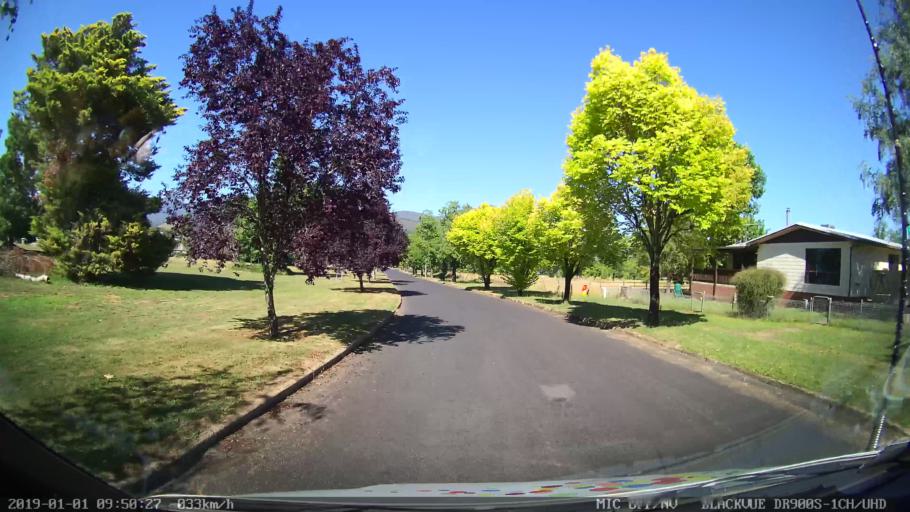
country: AU
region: New South Wales
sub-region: Snowy River
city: Jindabyne
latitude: -36.2164
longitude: 148.1261
